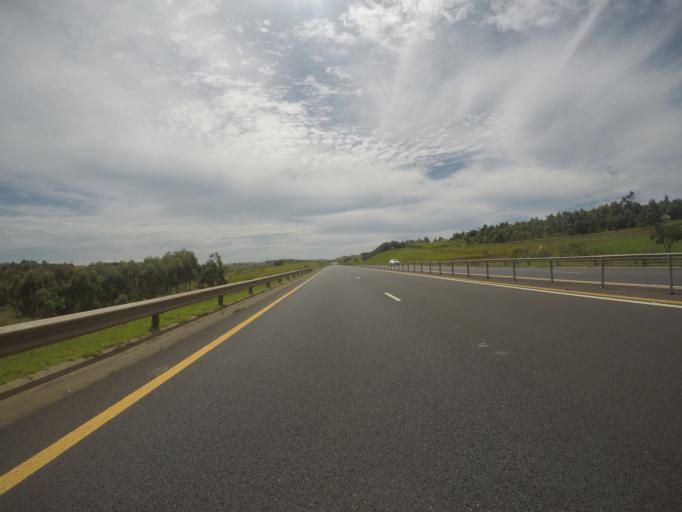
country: ZA
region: KwaZulu-Natal
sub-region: iLembe District Municipality
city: Mandeni
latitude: -29.1811
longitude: 31.4931
